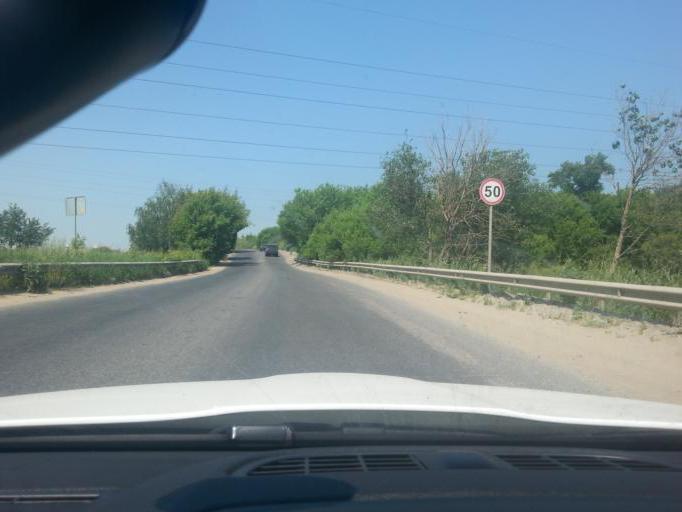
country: RU
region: Moscow
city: Nekrasovka
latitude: 55.7115
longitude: 37.9522
